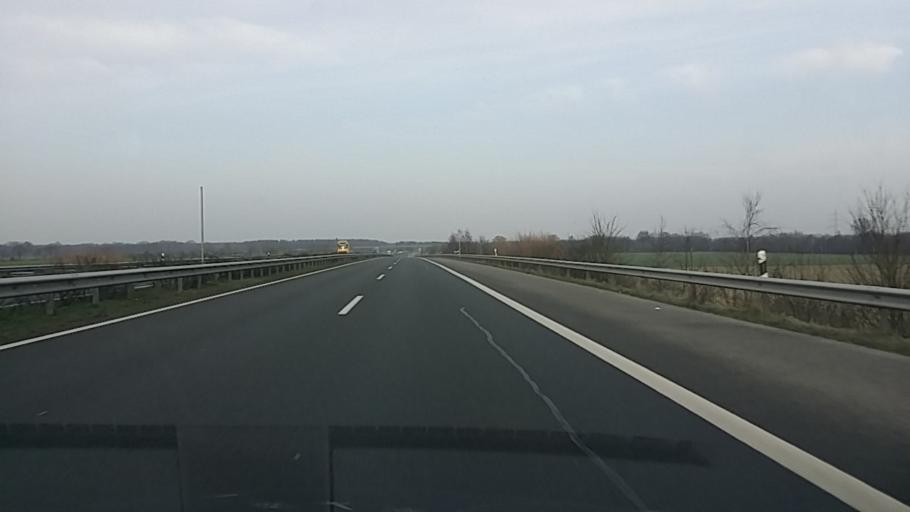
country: DE
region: Lower Saxony
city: Schuttorf
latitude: 52.3701
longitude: 7.2522
